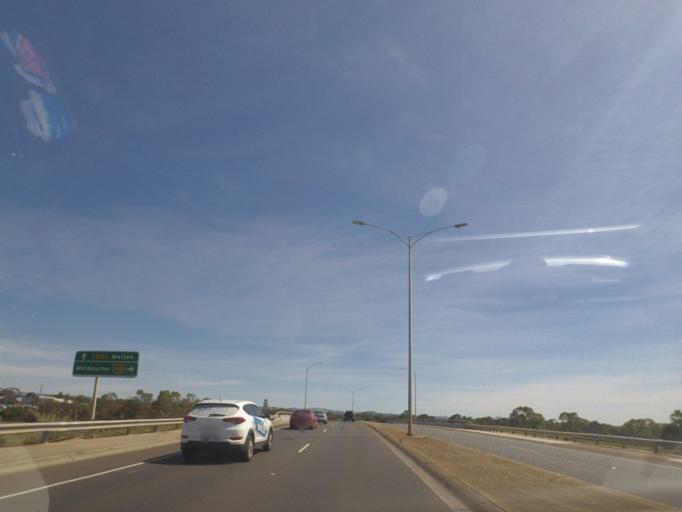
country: AU
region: Victoria
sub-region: Melton
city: Brookfield
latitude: -37.6911
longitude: 144.5669
